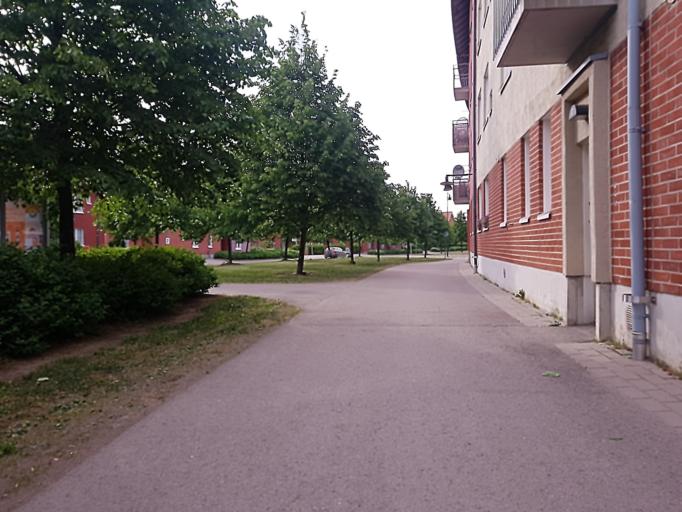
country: FI
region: Uusimaa
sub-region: Helsinki
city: Vantaa
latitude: 60.2819
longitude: 24.9602
